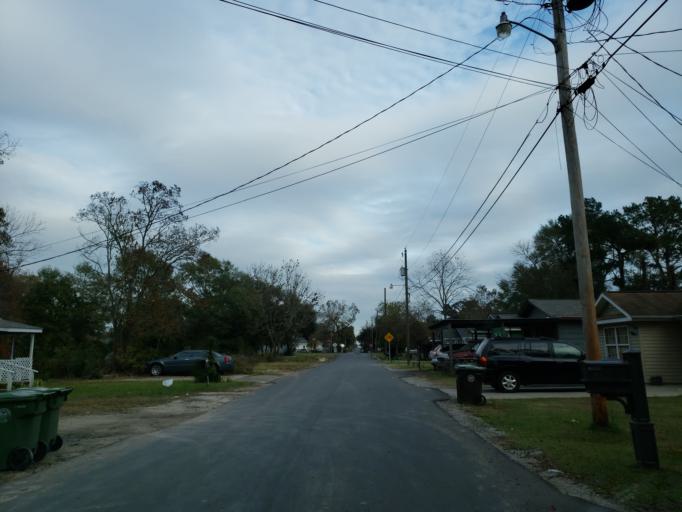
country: US
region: Mississippi
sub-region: Forrest County
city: Hattiesburg
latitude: 31.3120
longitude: -89.2883
